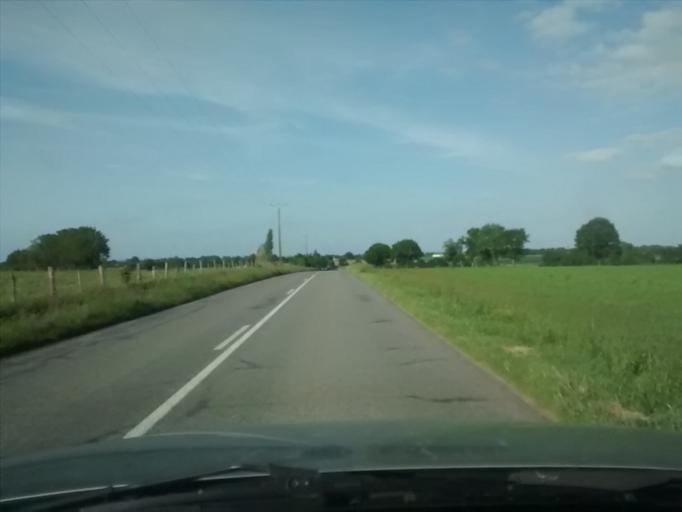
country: FR
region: Pays de la Loire
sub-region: Departement de la Mayenne
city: Meslay-du-Maine
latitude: 47.9441
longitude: -0.6361
